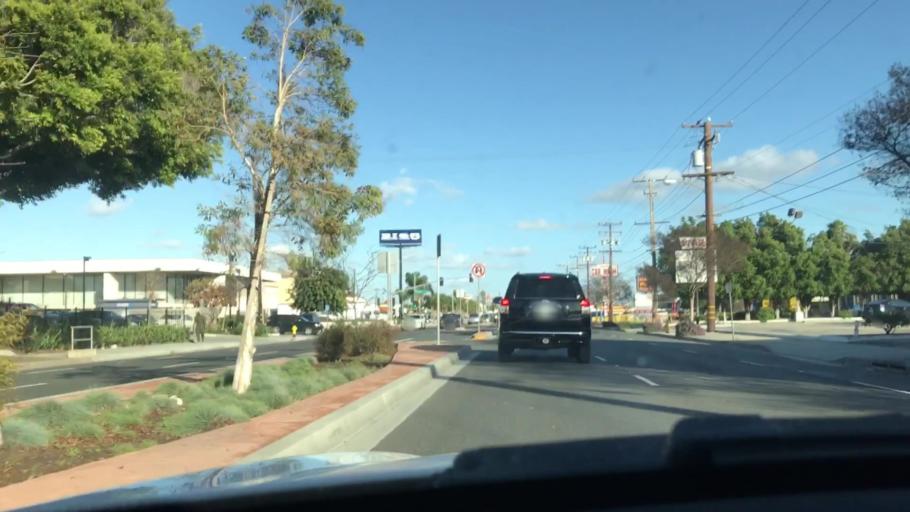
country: US
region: California
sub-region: Los Angeles County
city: Alondra Park
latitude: 33.9019
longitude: -118.3222
